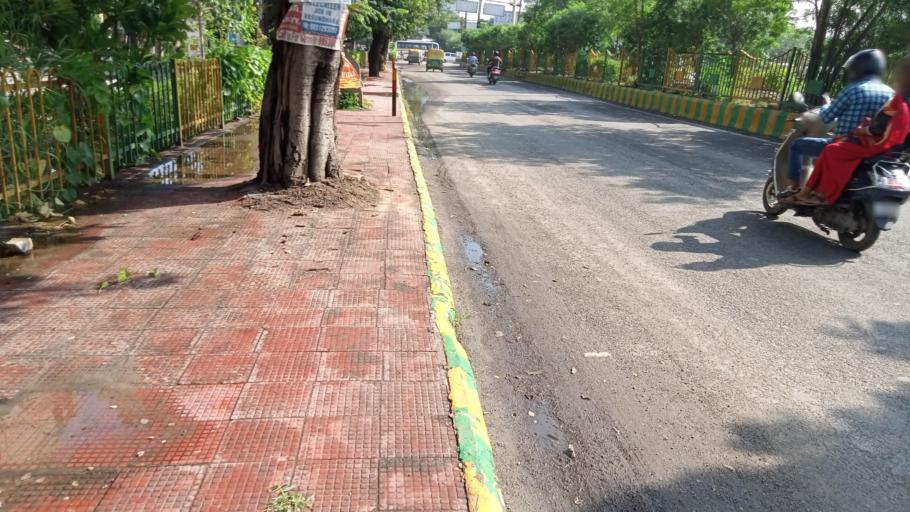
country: IN
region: Uttar Pradesh
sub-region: Ghaziabad
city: Ghaziabad
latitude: 28.6633
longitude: 77.3730
